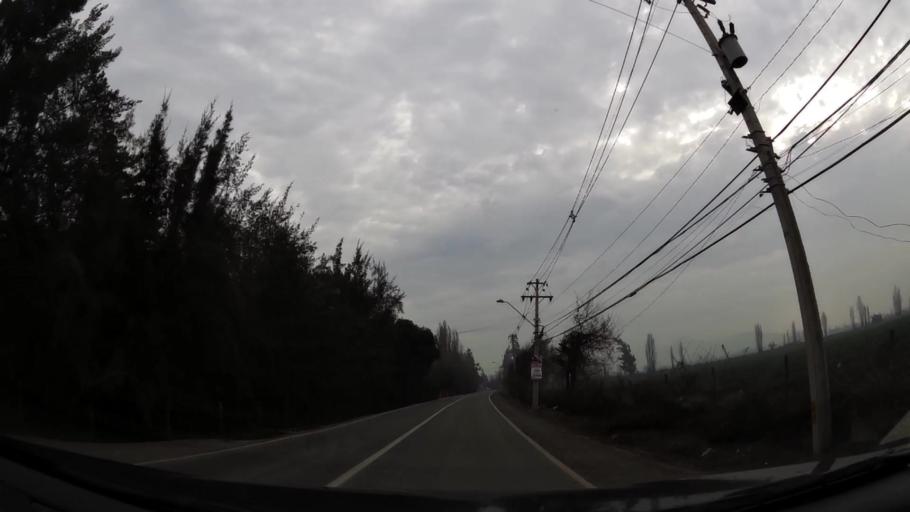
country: CL
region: Santiago Metropolitan
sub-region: Provincia de Chacabuco
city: Chicureo Abajo
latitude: -33.2502
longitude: -70.7636
